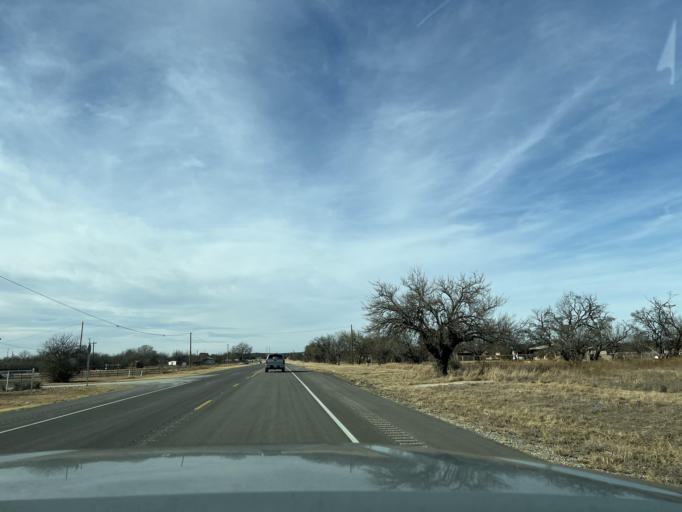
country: US
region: Texas
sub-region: Shackelford County
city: Albany
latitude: 32.7161
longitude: -99.2842
